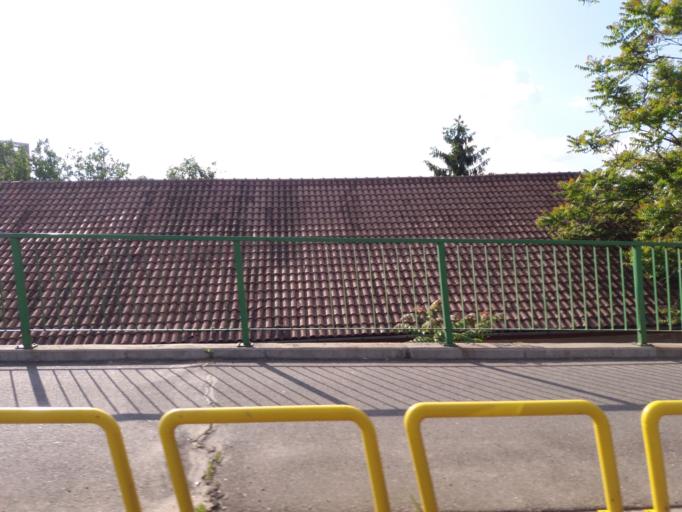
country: RO
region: Arad
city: Arad
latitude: 46.1882
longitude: 21.3283
